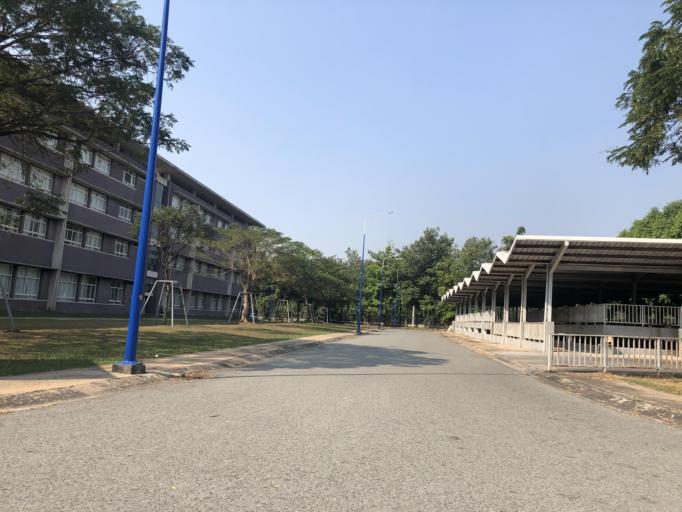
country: VN
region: Binh Duong
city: Thu Dau Mot
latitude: 11.0548
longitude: 106.6655
